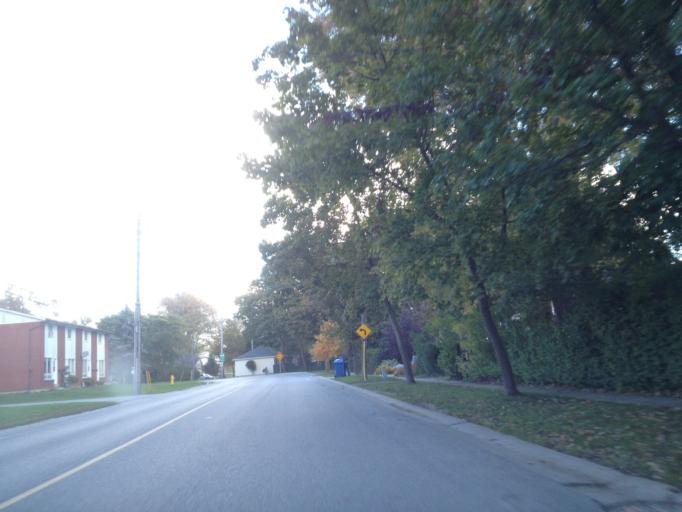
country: CA
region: Ontario
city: Amherstburg
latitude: 42.0300
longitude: -82.7288
